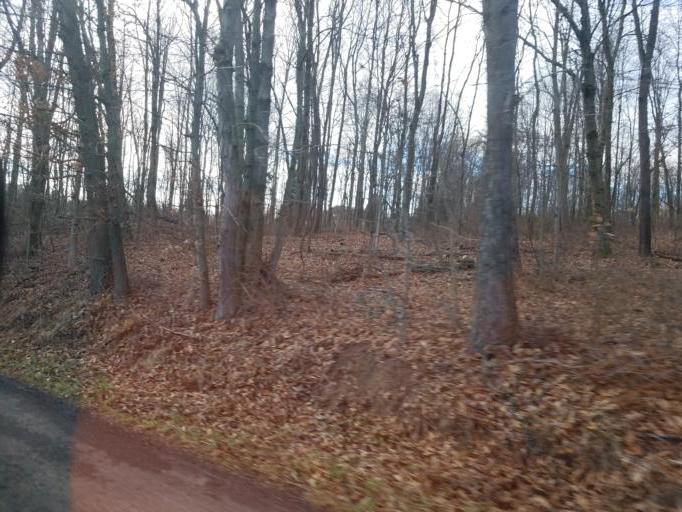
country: US
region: Ohio
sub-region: Sandusky County
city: Bellville
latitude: 40.5826
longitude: -82.3746
